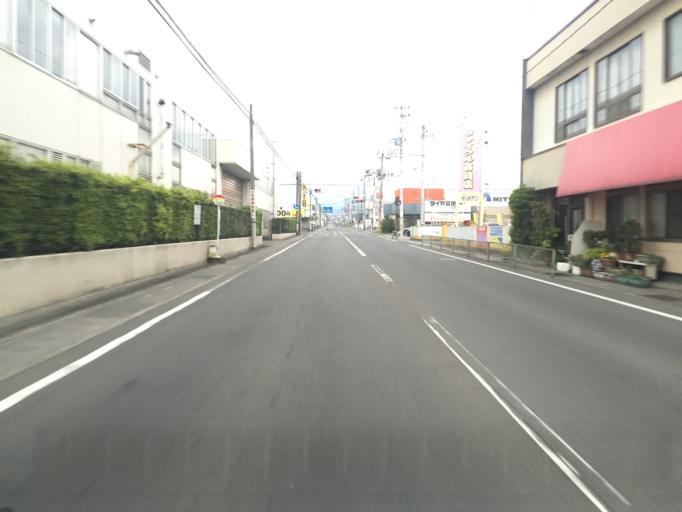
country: JP
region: Fukushima
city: Fukushima-shi
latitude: 37.7442
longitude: 140.4485
